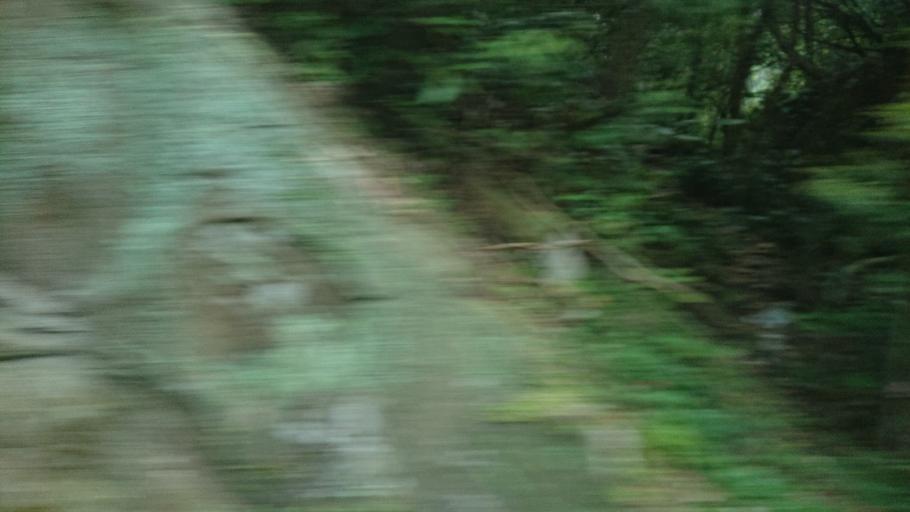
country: TW
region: Taiwan
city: Daxi
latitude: 24.8814
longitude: 121.3799
